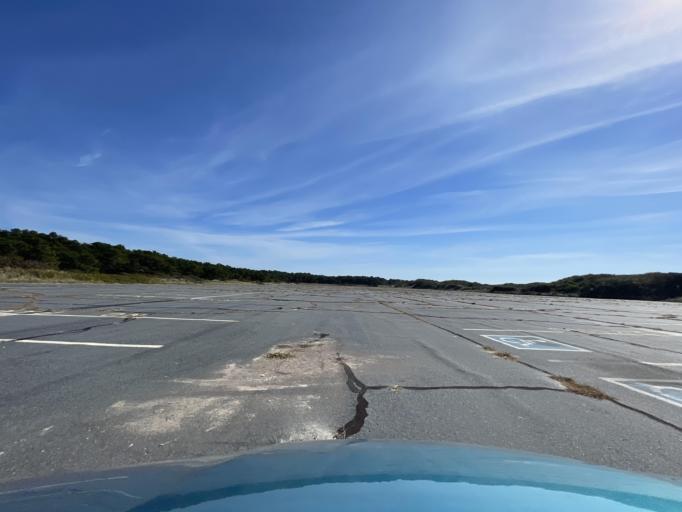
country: US
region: Massachusetts
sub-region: Bristol County
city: Head of Westport
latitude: 41.5059
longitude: -71.0506
